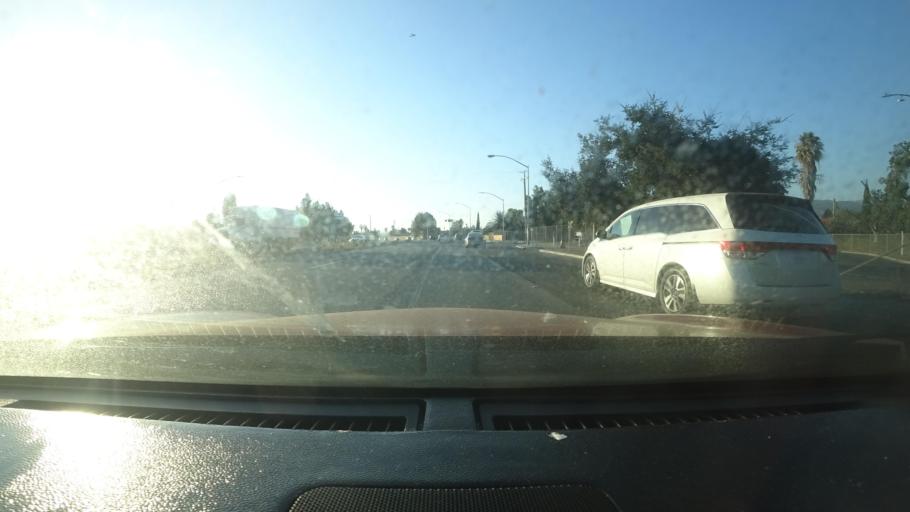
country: US
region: California
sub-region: Santa Clara County
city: Alum Rock
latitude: 37.3534
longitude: -121.8284
